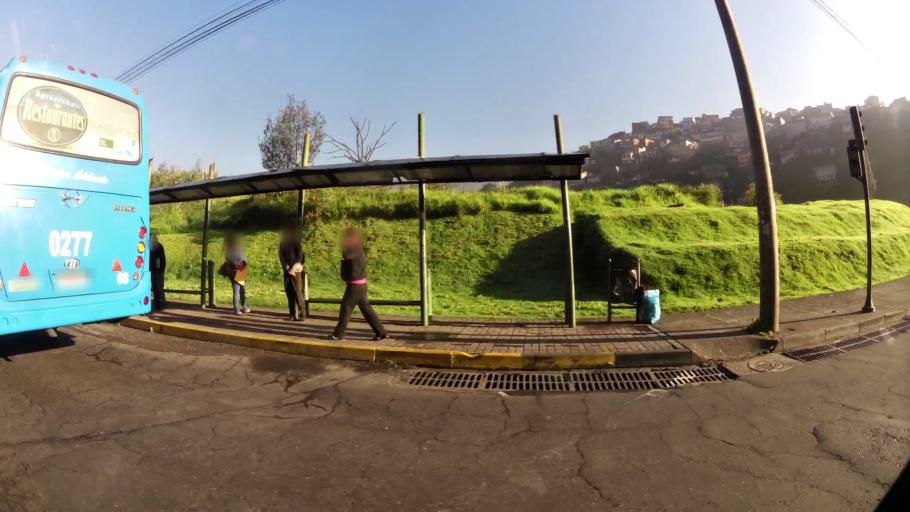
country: EC
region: Pichincha
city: Quito
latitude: -0.2321
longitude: -78.5046
